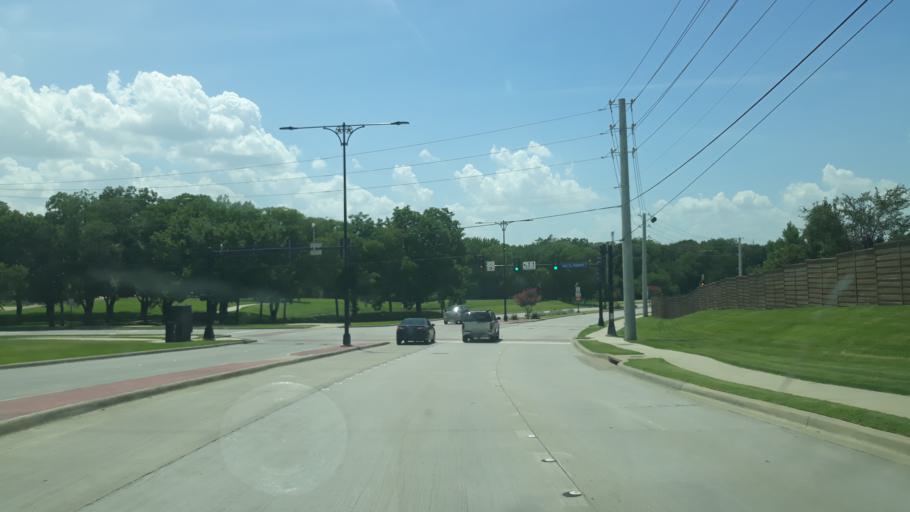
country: US
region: Texas
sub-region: Dallas County
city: Coppell
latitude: 32.9698
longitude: -97.0059
